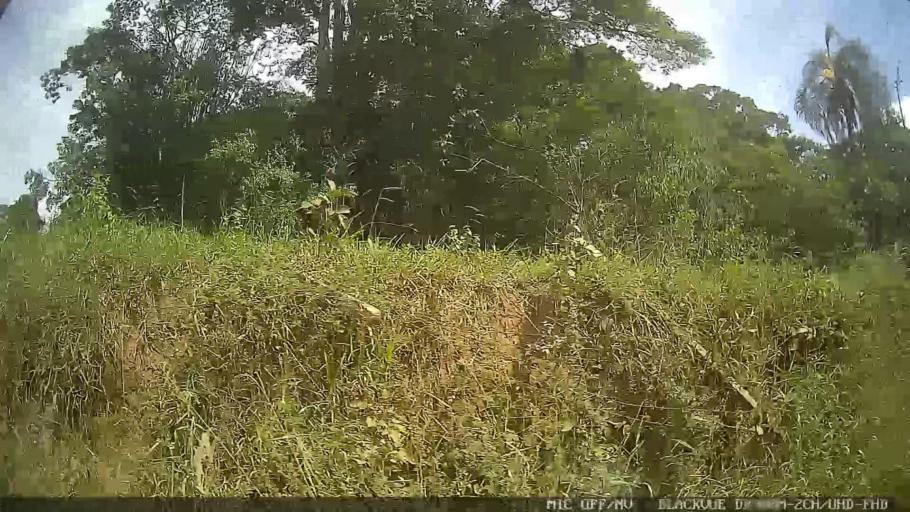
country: BR
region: Sao Paulo
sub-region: Atibaia
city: Atibaia
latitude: -23.0919
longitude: -46.5456
